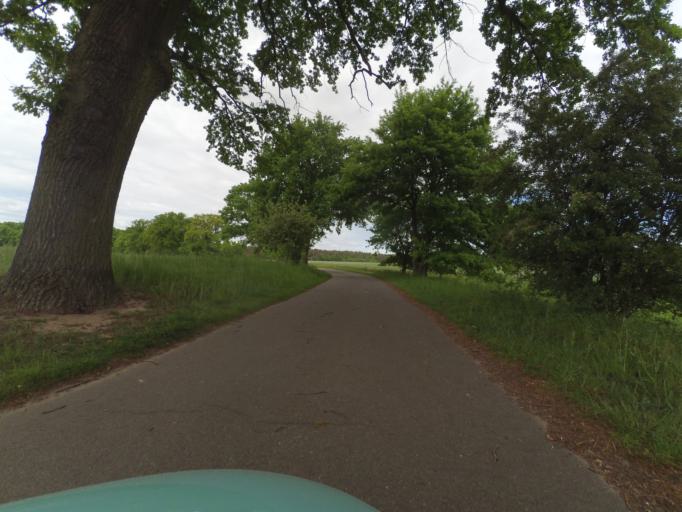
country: DE
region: Lower Saxony
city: Wunstorf
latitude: 52.4375
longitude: 9.4980
